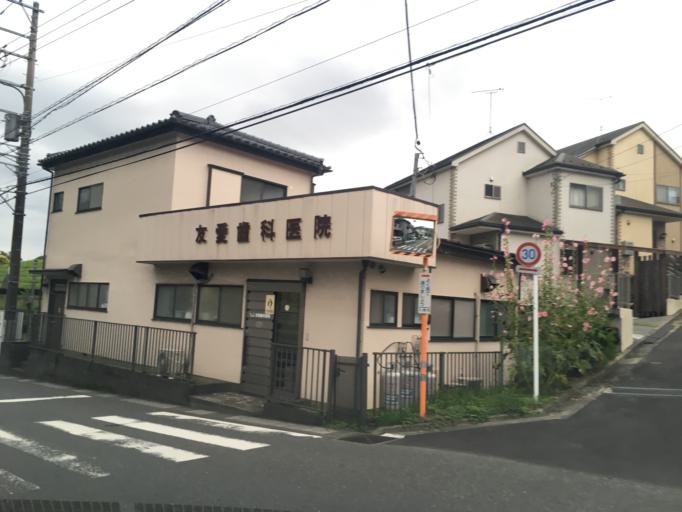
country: JP
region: Saitama
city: Sayama
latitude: 35.8311
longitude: 139.3673
